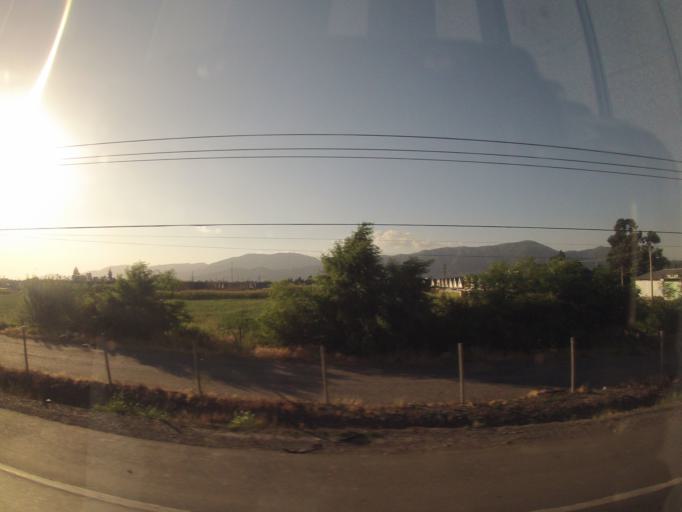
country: CL
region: O'Higgins
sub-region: Provincia de Colchagua
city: Chimbarongo
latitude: -34.5992
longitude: -70.9771
